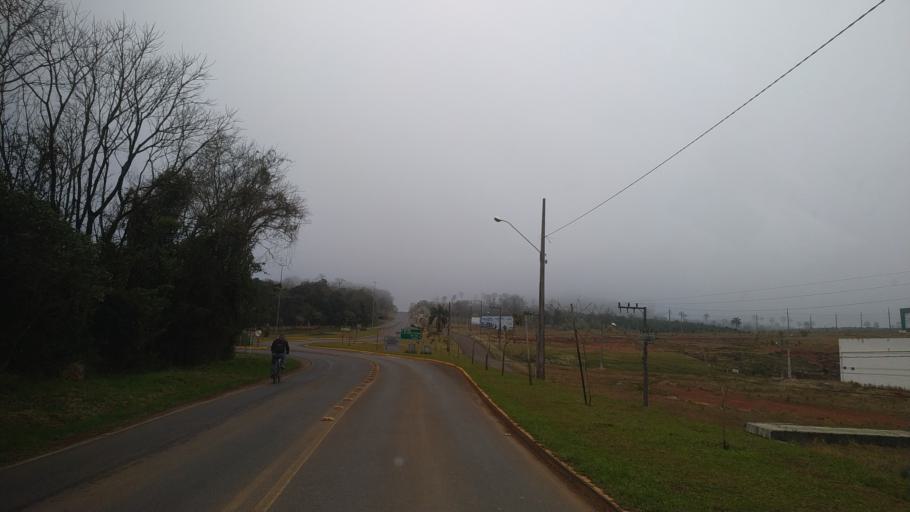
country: BR
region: Santa Catarina
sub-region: Chapeco
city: Chapeco
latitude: -27.1369
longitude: -52.6294
